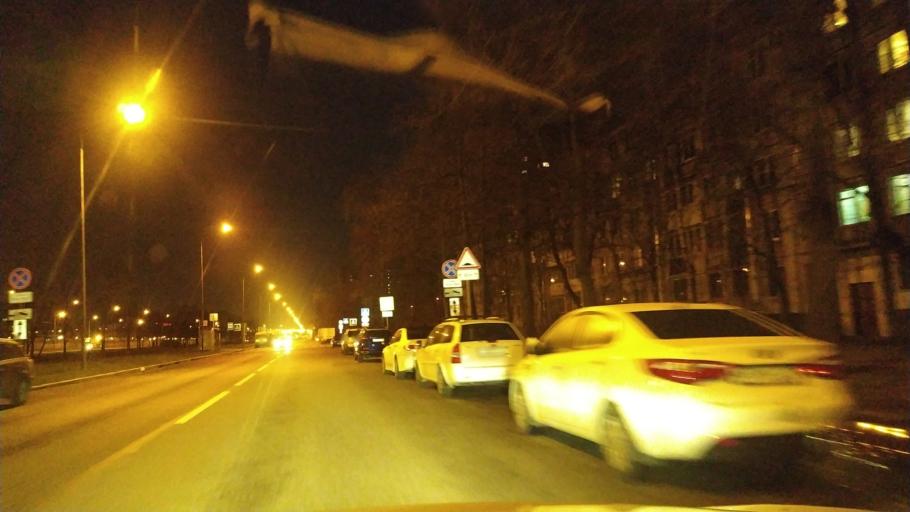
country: RU
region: St.-Petersburg
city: Kupchino
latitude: 59.8428
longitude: 30.3673
